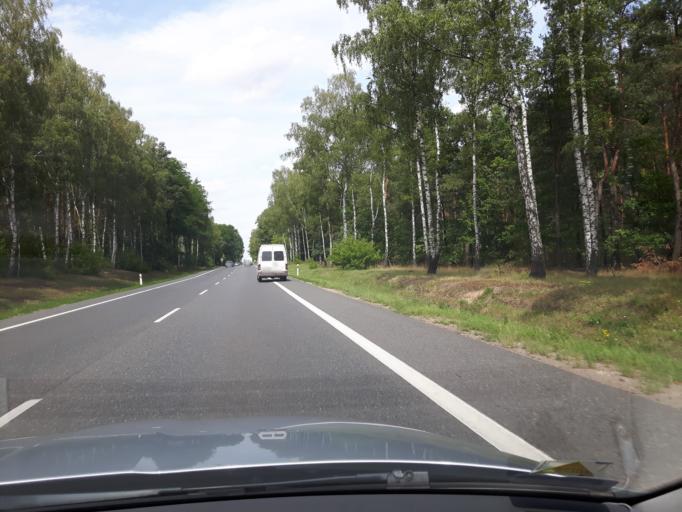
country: PL
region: Masovian Voivodeship
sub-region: Powiat mlawski
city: Strzegowo
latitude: 52.9117
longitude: 20.2866
